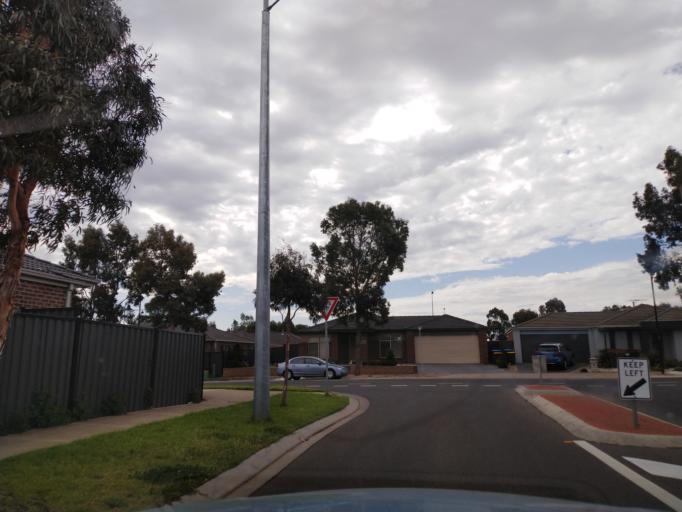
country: AU
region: Victoria
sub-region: Wyndham
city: Williams Landing
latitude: -37.8424
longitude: 144.7165
